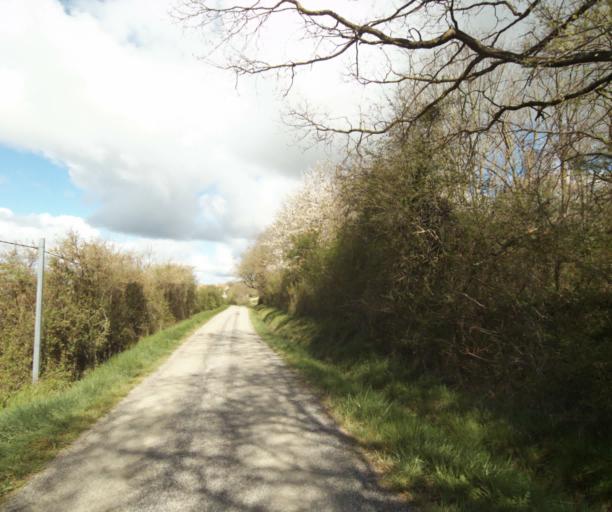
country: FR
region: Midi-Pyrenees
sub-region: Departement de l'Ariege
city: Saverdun
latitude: 43.1856
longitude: 1.5399
